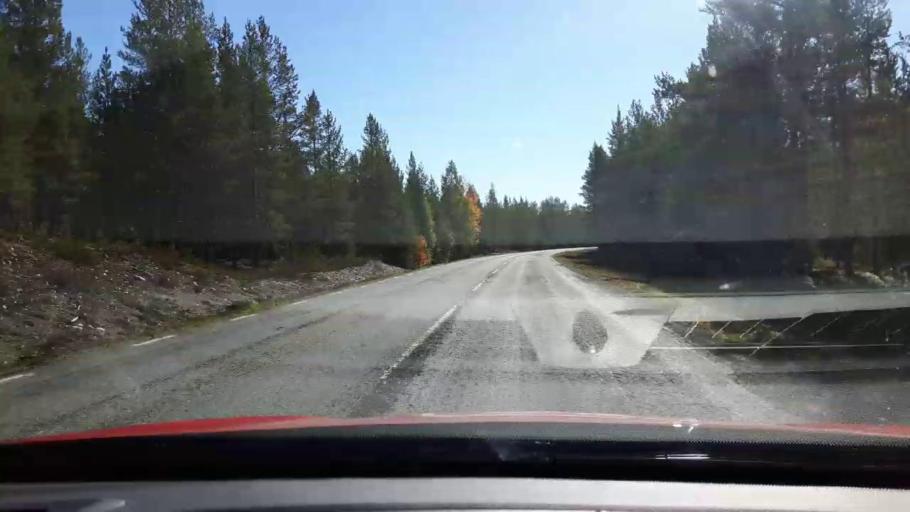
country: SE
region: Jaemtland
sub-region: Harjedalens Kommun
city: Sveg
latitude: 62.4232
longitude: 13.9038
